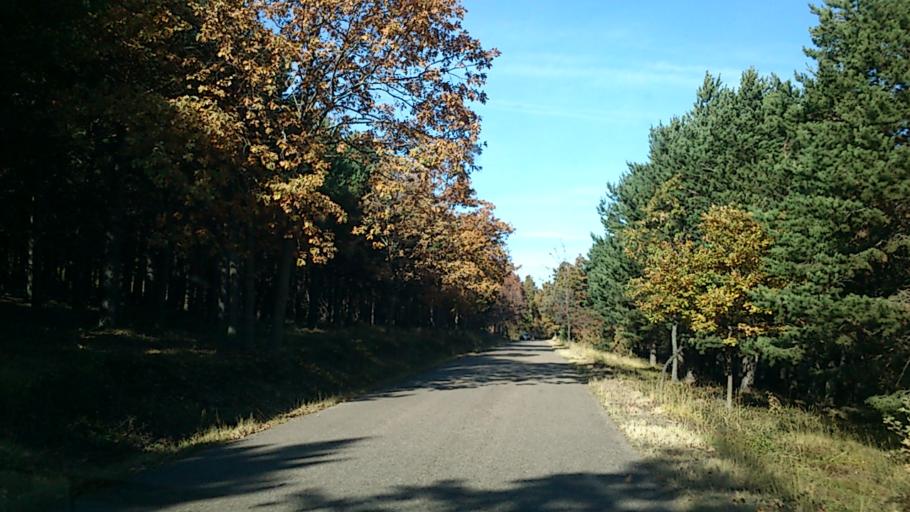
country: ES
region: Aragon
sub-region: Provincia de Zaragoza
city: Litago
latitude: 41.8049
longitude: -1.7922
